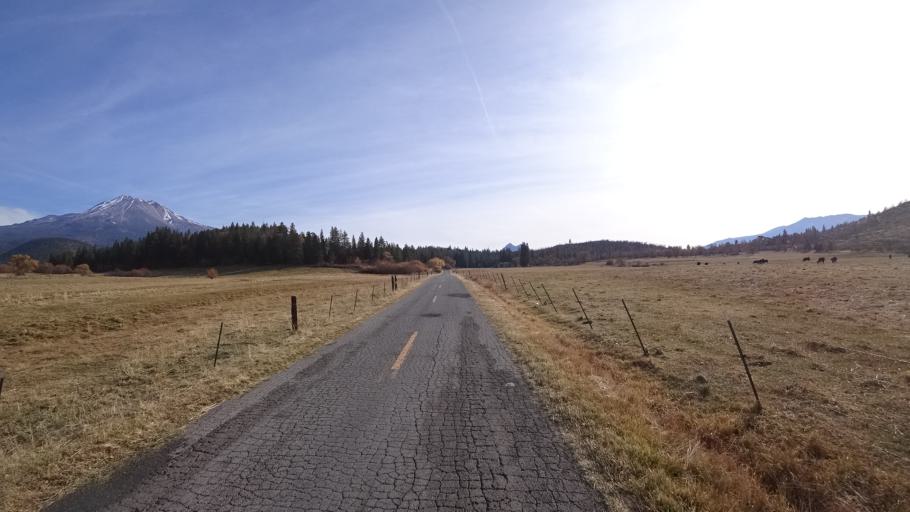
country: US
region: California
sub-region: Siskiyou County
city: Weed
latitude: 41.4528
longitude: -122.3829
